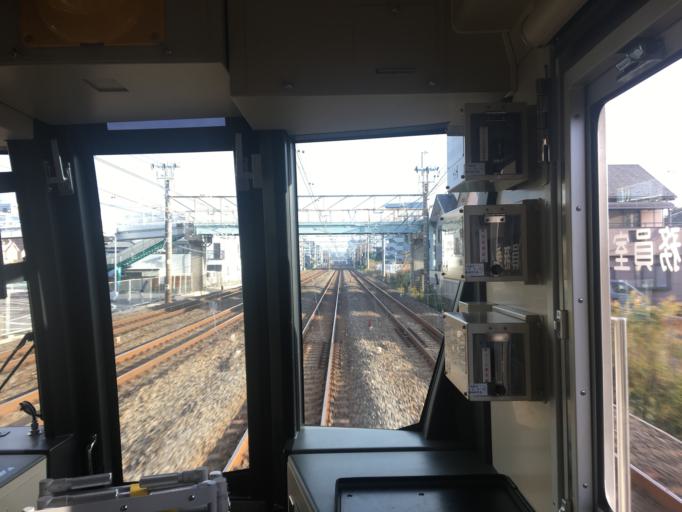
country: JP
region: Chiba
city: Kashiwa
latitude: 35.8515
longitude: 139.9626
